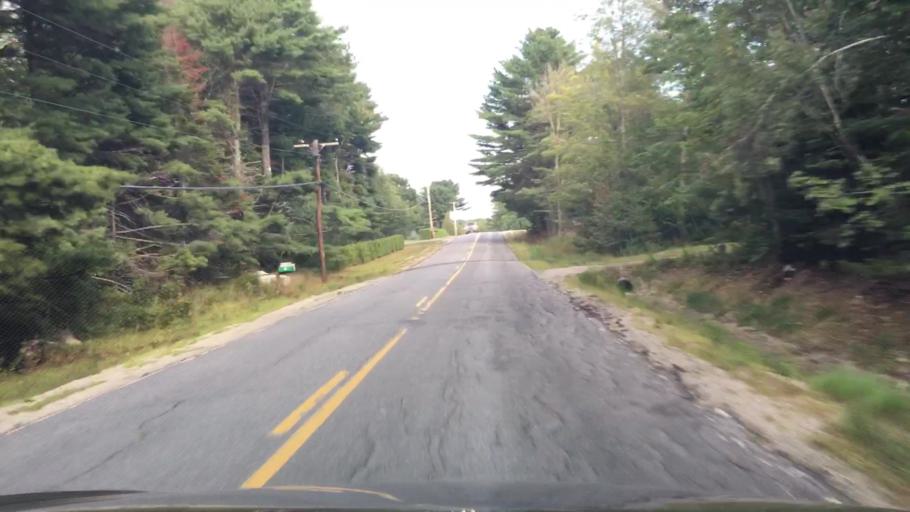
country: US
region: Maine
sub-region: Hancock County
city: Surry
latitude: 44.4996
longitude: -68.5548
